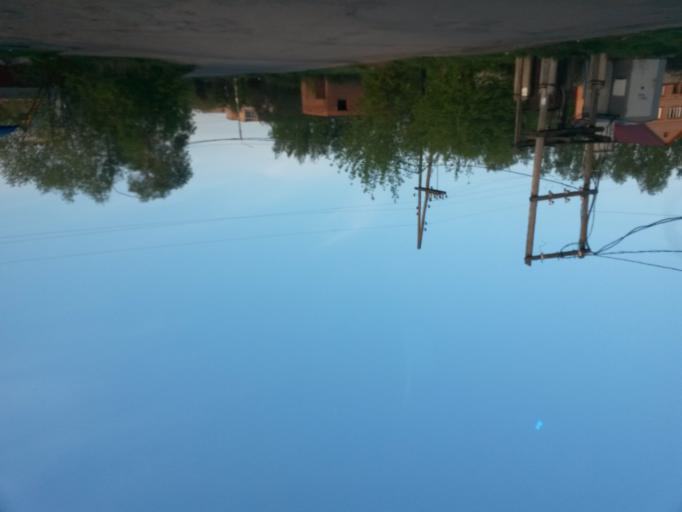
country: RU
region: Moskovskaya
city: Lyubuchany
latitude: 55.2375
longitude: 37.5438
